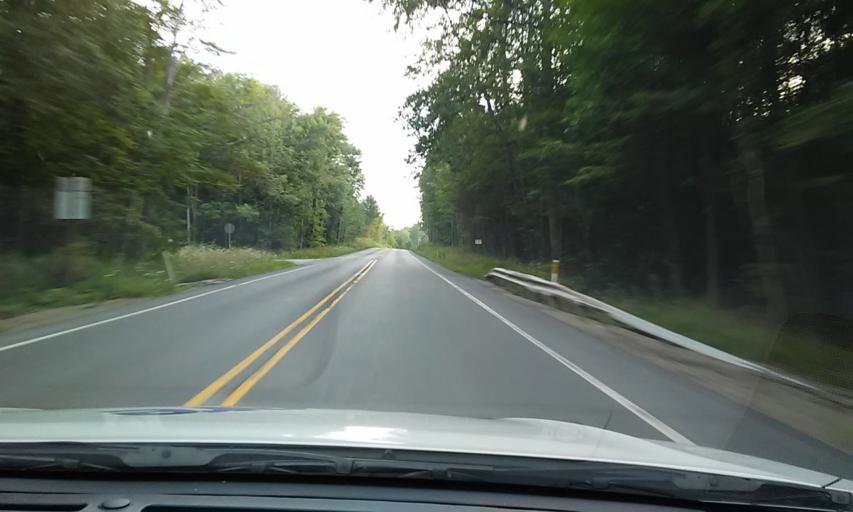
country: US
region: Pennsylvania
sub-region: McKean County
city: Kane
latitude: 41.5858
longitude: -78.8471
